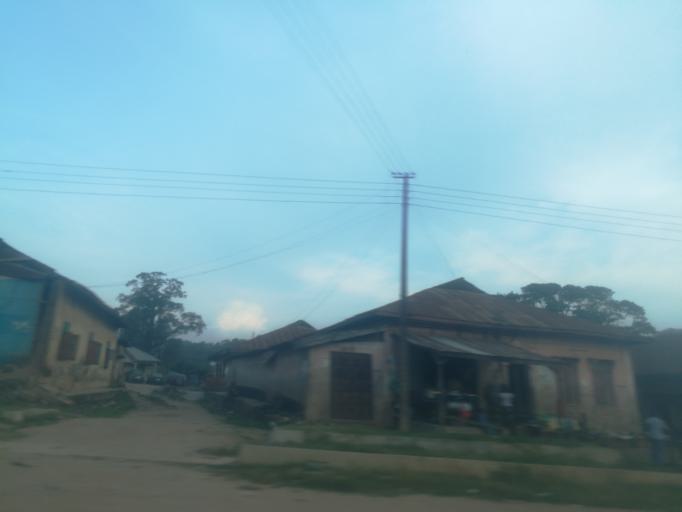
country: NG
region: Ogun
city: Abeokuta
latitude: 7.1744
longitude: 3.3394
